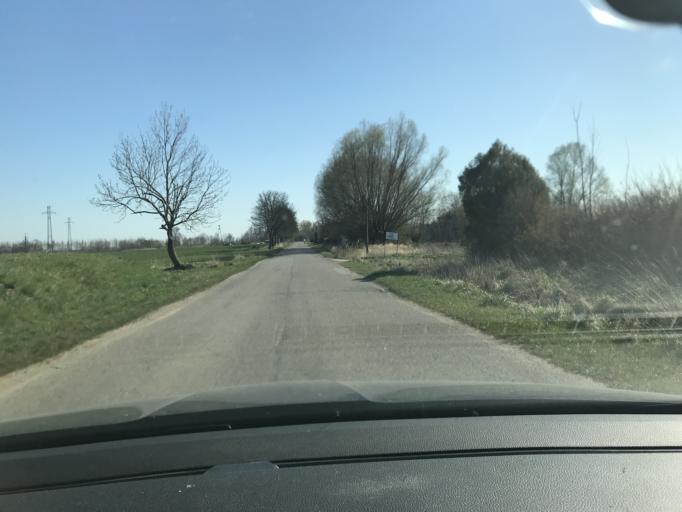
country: PL
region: Pomeranian Voivodeship
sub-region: Powiat nowodworski
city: Sztutowo
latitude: 54.3157
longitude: 19.1596
